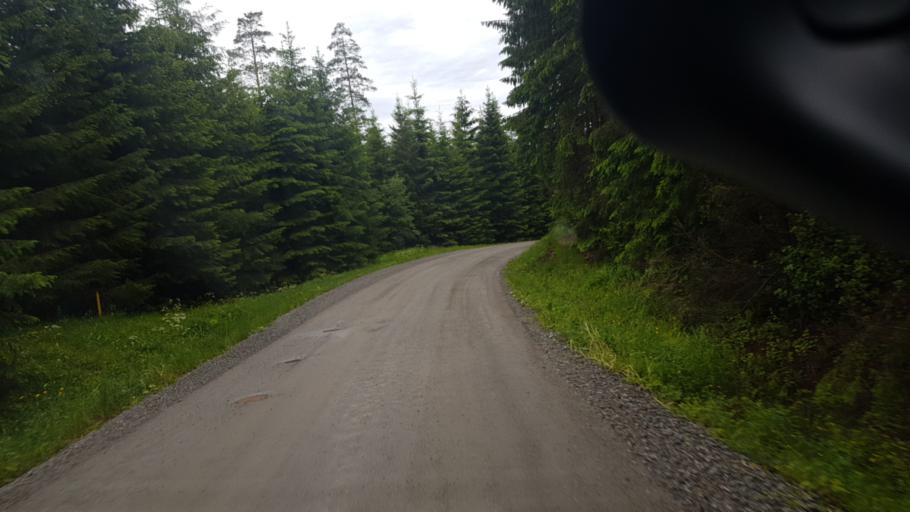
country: NO
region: Ostfold
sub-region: Romskog
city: Romskog
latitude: 59.6942
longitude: 11.9429
